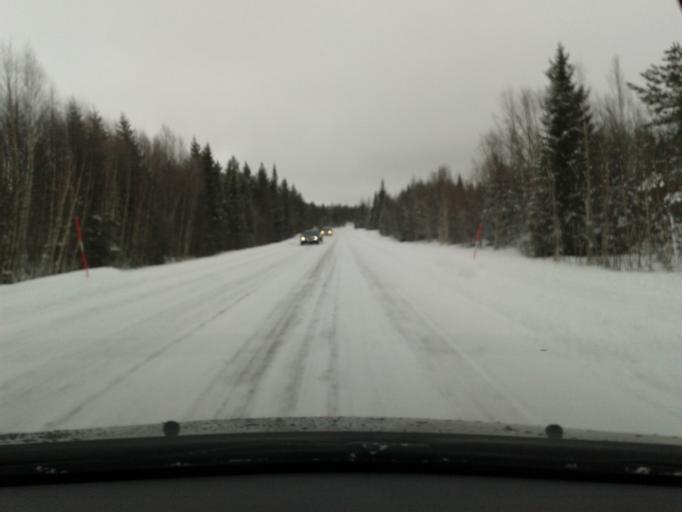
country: SE
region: Vaesterbotten
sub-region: Vilhelmina Kommun
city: Sjoberg
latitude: 64.8725
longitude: 15.8856
